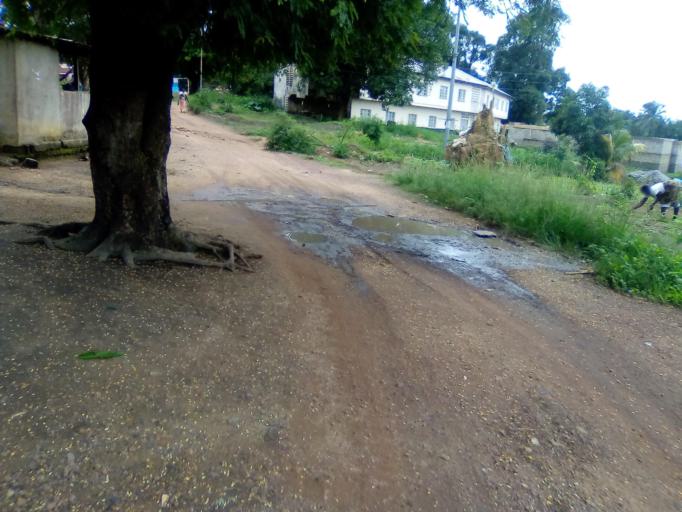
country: SL
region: Southern Province
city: Bo
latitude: 7.9475
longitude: -11.7265
